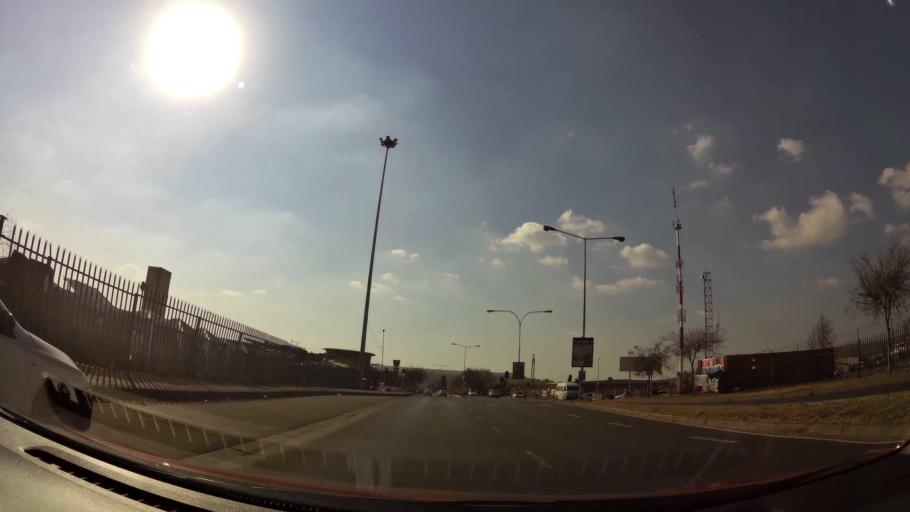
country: ZA
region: Gauteng
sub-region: City of Johannesburg Metropolitan Municipality
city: Soweto
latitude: -26.2435
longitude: 27.9495
